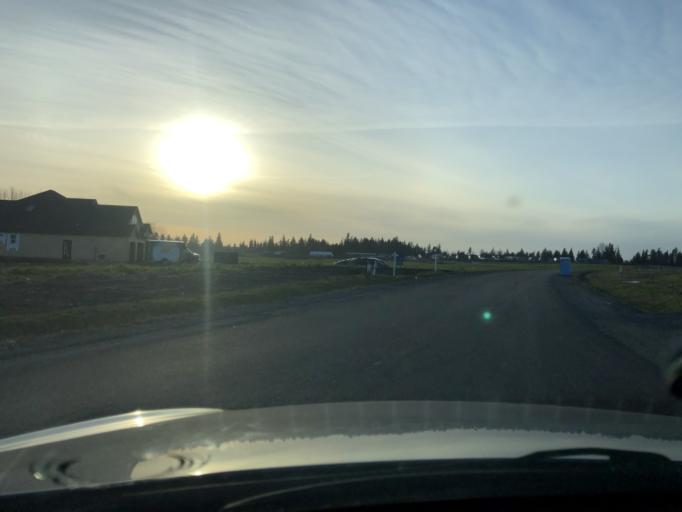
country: US
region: Washington
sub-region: Pierce County
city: Prairie Ridge
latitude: 47.1935
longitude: -122.1128
